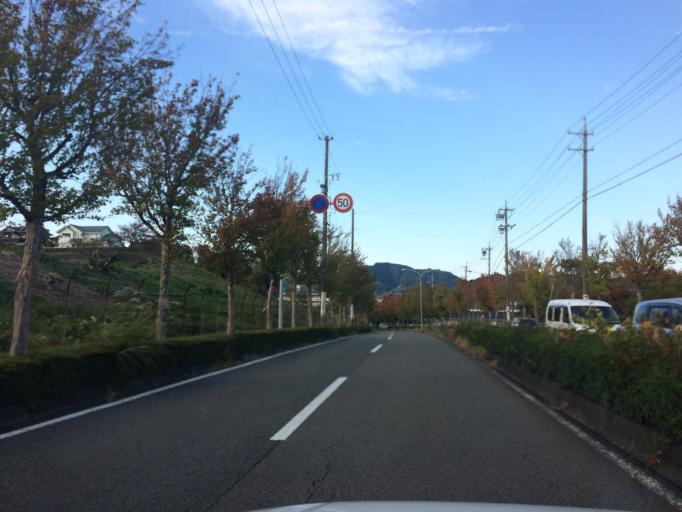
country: JP
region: Shizuoka
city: Fujieda
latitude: 34.8626
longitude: 138.2399
